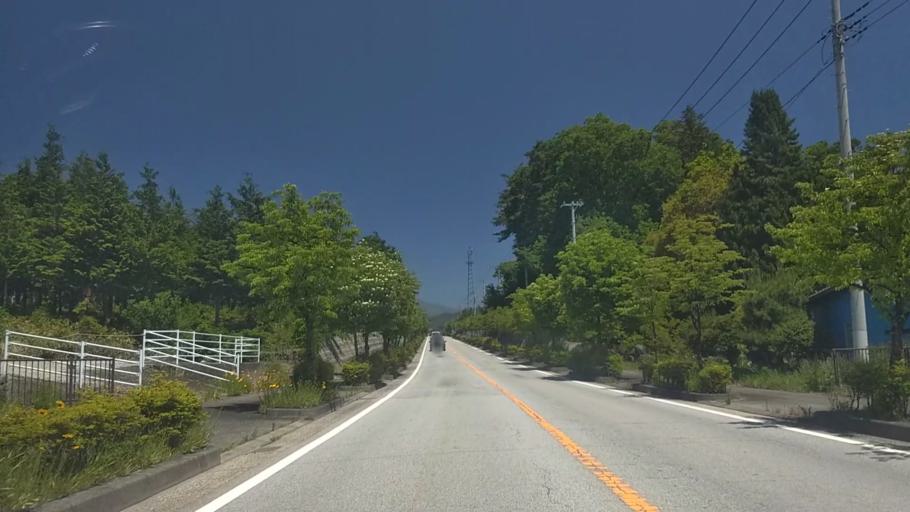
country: JP
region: Yamanashi
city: Nirasaki
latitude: 35.8180
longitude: 138.4294
